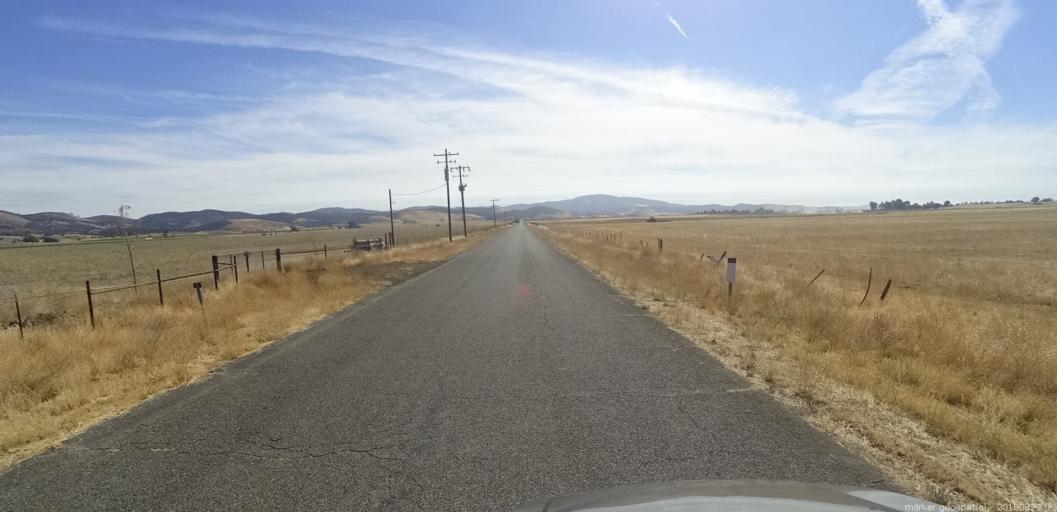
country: US
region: California
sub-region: Monterey County
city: King City
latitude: 35.9659
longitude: -121.1162
